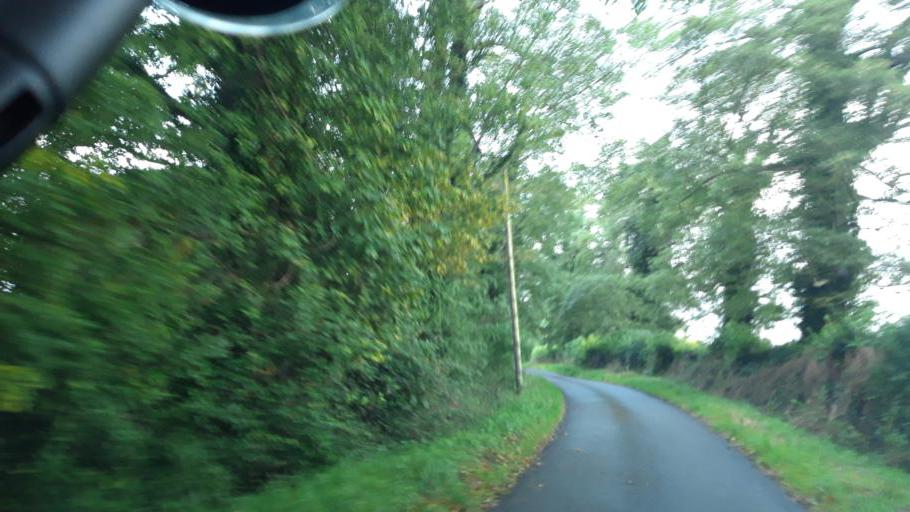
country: IE
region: Leinster
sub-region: Kildare
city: Leixlip
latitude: 53.3440
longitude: -6.4847
